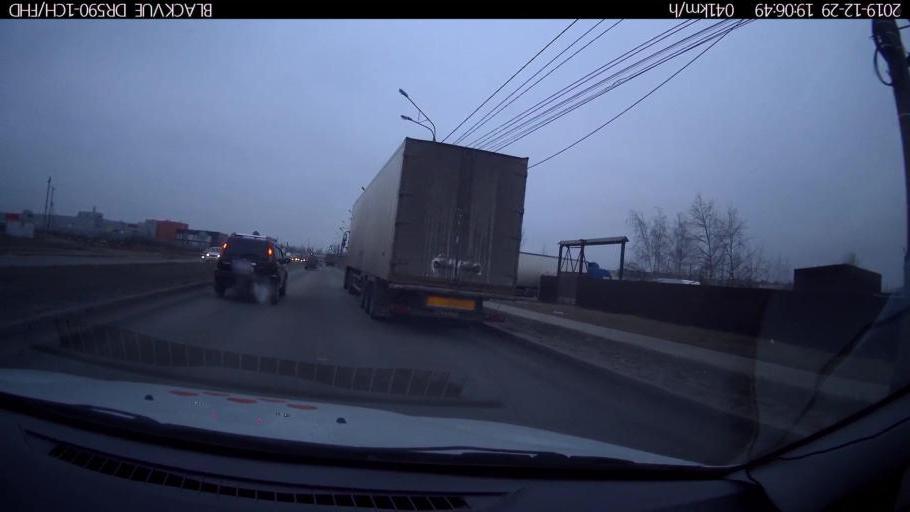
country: RU
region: Nizjnij Novgorod
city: Neklyudovo
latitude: 56.3438
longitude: 43.8890
